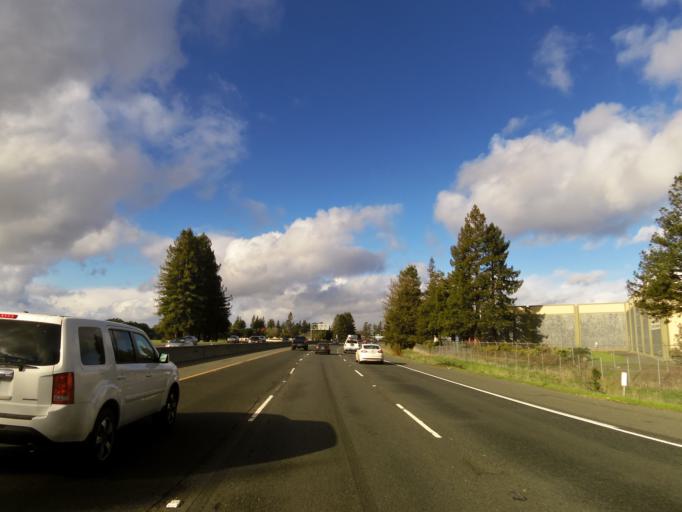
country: US
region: California
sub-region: Sonoma County
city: Rohnert Park
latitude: 38.3723
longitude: -122.7145
